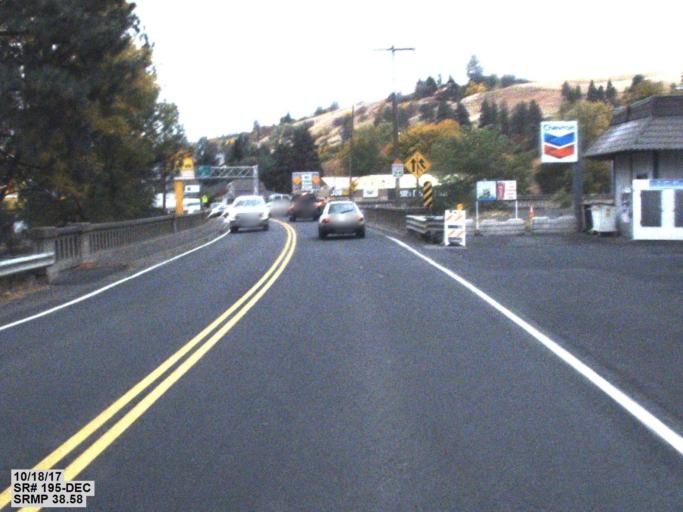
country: US
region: Washington
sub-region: Whitman County
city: Colfax
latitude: 46.8910
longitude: -117.3636
